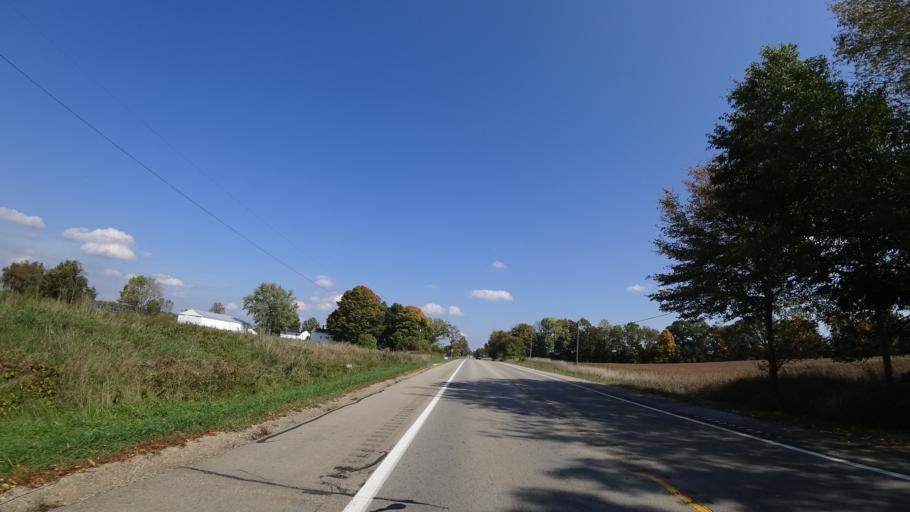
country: US
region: Michigan
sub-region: Jackson County
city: Concord
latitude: 42.1869
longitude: -84.6327
